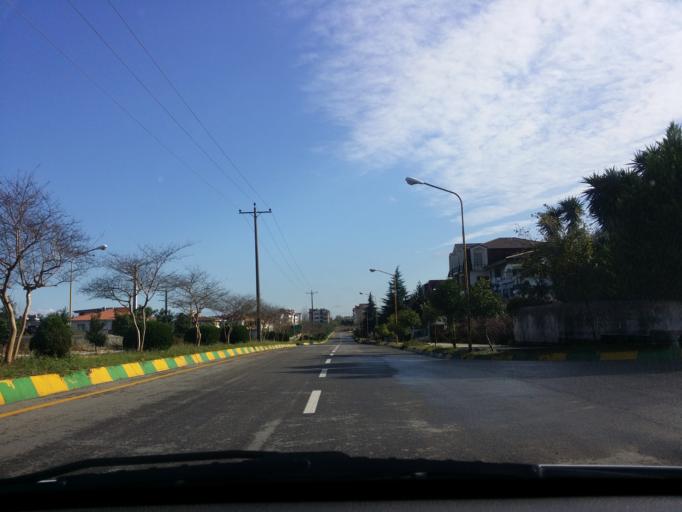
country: IR
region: Mazandaran
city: Chalus
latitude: 36.6667
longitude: 51.3131
